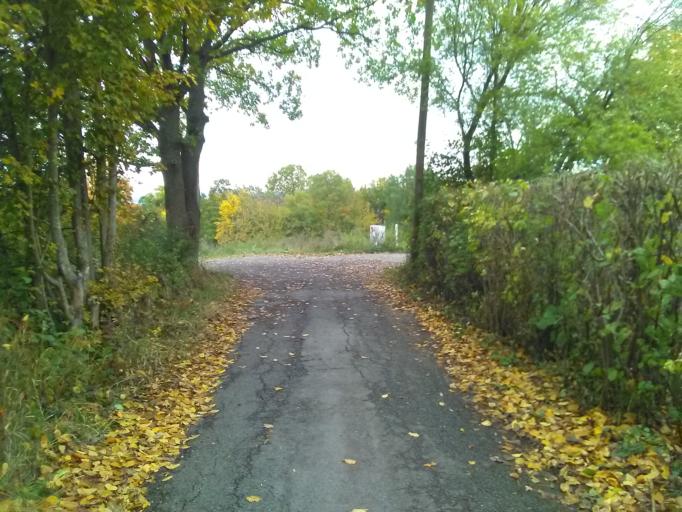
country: DE
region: Bavaria
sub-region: Upper Franconia
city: Bamberg
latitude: 49.8831
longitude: 10.8920
